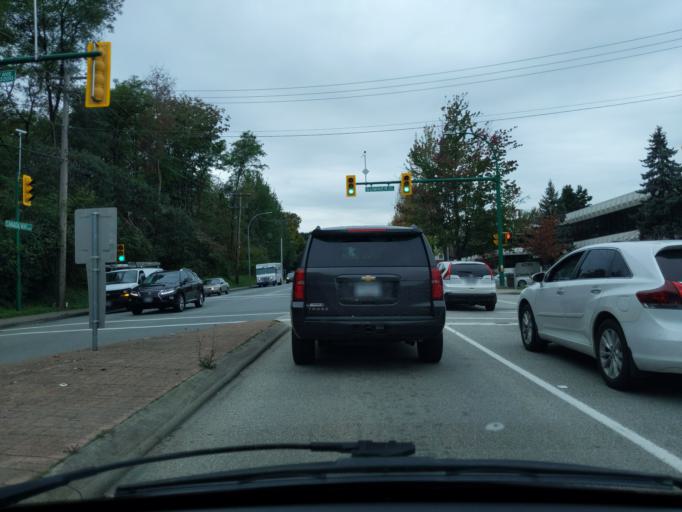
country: CA
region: British Columbia
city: Burnaby
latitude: 49.2547
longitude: -123.0080
